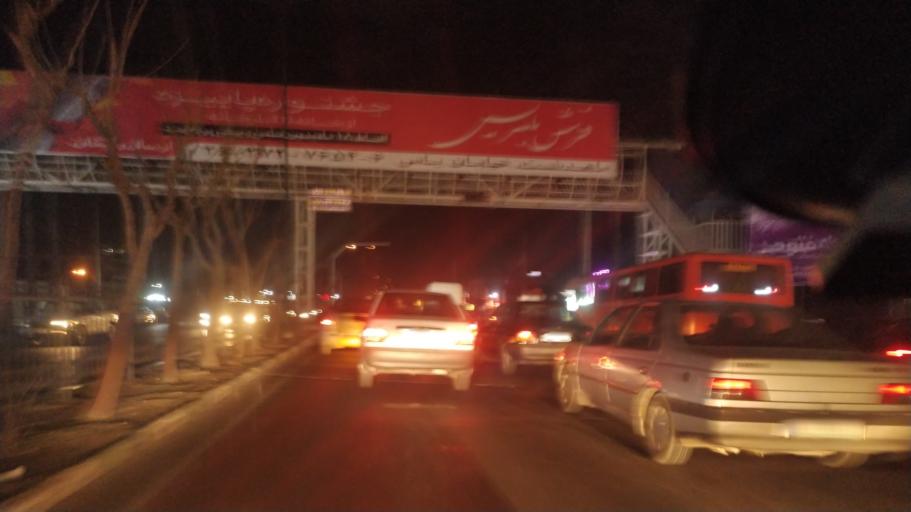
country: IR
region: Alborz
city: Karaj
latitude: 35.7796
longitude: 51.0061
